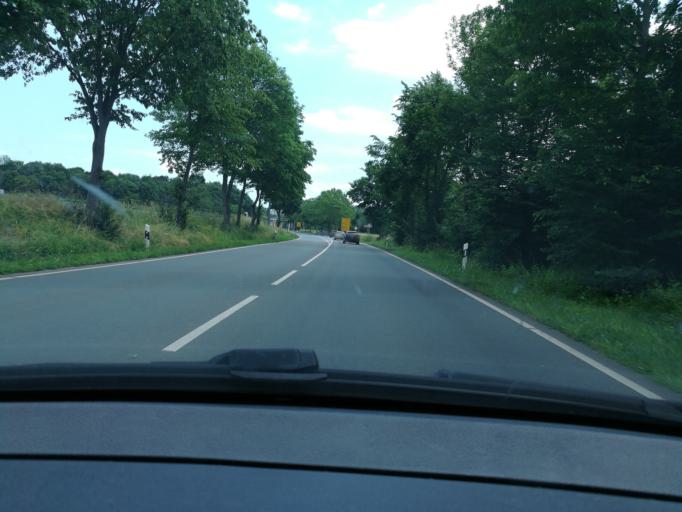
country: DE
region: North Rhine-Westphalia
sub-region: Regierungsbezirk Detmold
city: Petershagen
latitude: 52.3098
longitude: 8.9795
